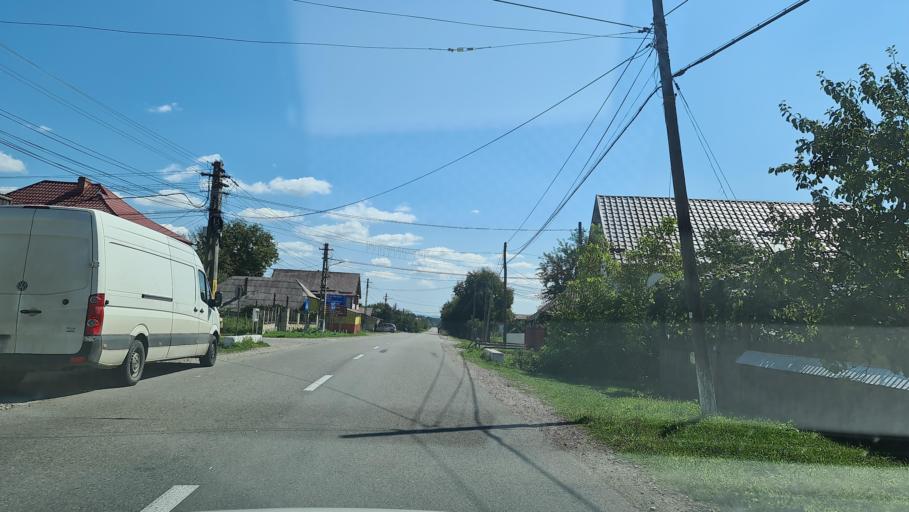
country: RO
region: Bacau
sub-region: Comuna Balcani
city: Balcani
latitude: 46.6462
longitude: 26.5661
